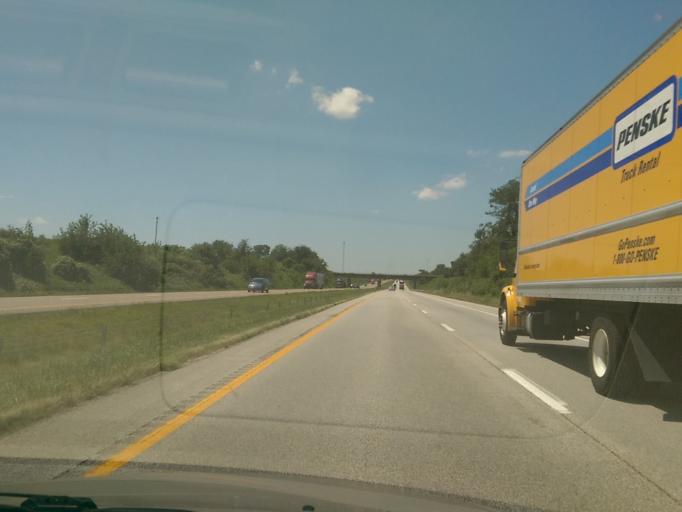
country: US
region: Missouri
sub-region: Cooper County
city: Boonville
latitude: 38.9353
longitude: -92.7978
